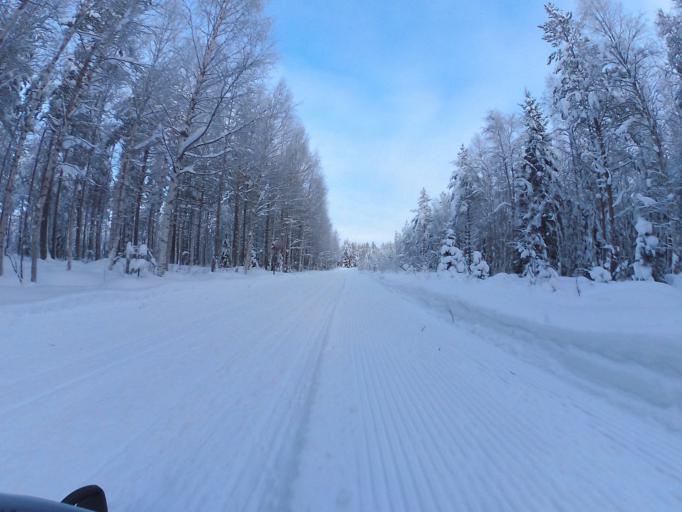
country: FI
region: Lapland
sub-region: Rovaniemi
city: Rovaniemi
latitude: 66.5293
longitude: 26.0340
